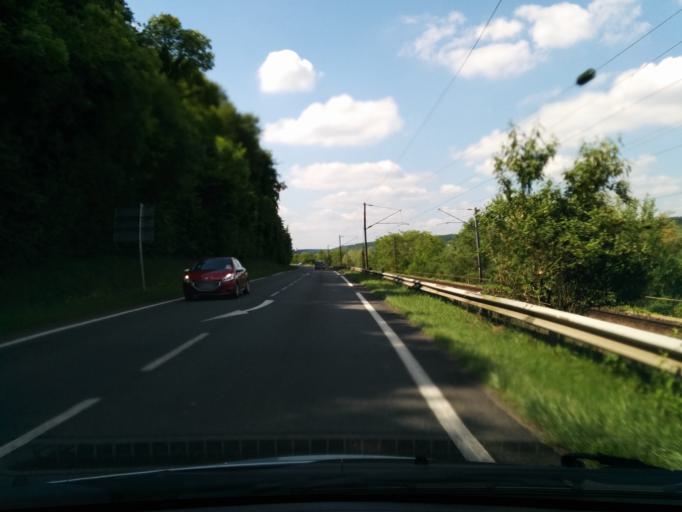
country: FR
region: Ile-de-France
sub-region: Departement des Yvelines
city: Limetz-Villez
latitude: 49.0685
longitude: 1.5186
